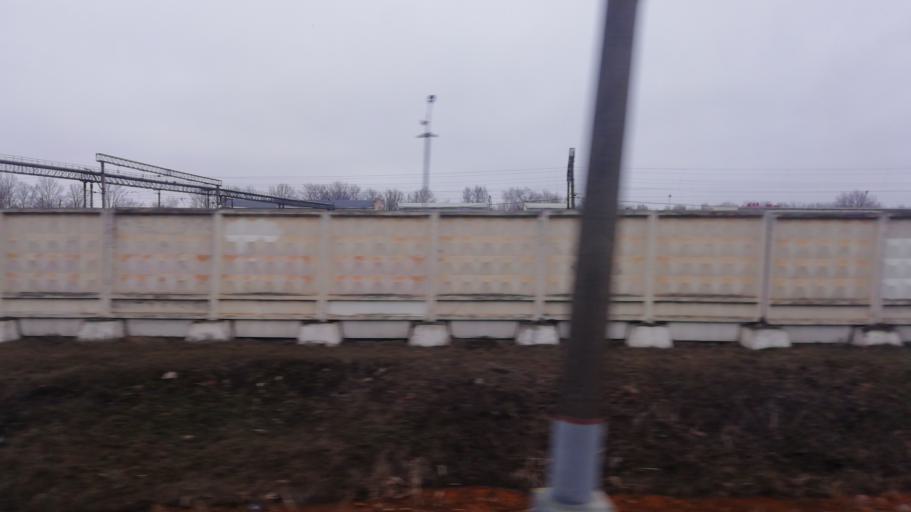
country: RU
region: St.-Petersburg
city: Kupchino
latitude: 59.8853
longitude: 30.3458
